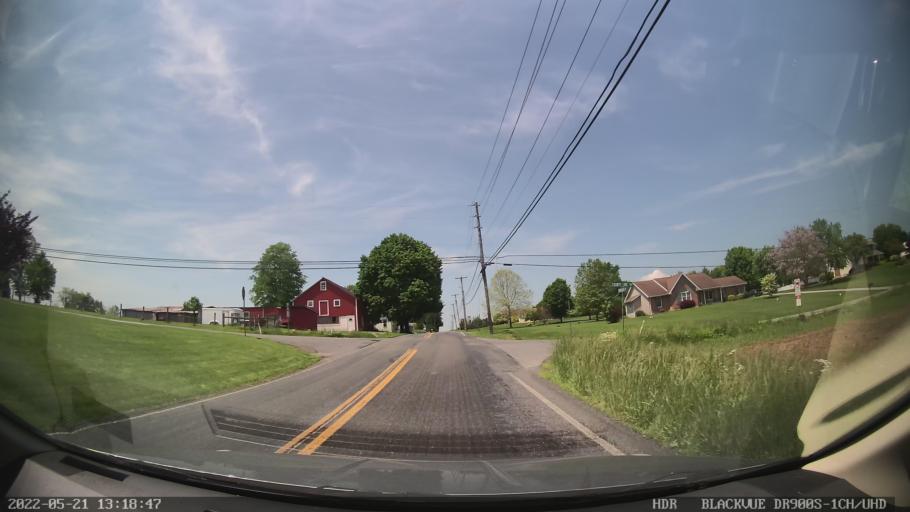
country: US
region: Pennsylvania
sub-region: Berks County
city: Bally
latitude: 40.3695
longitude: -75.5963
